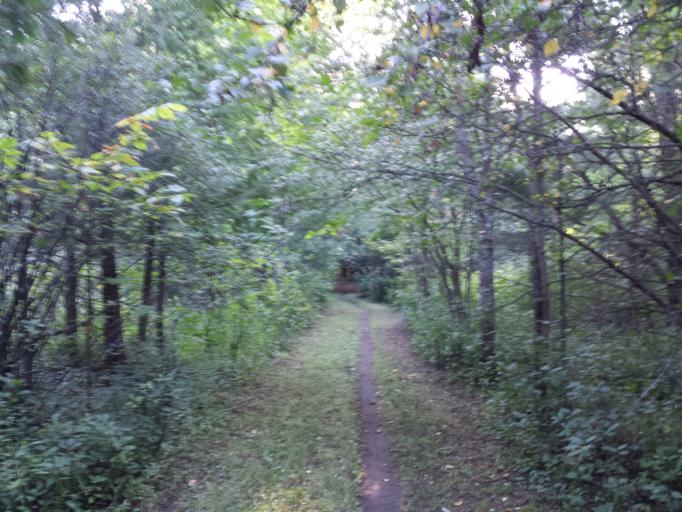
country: CA
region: Ontario
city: Bells Corners
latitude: 45.3167
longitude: -75.8574
